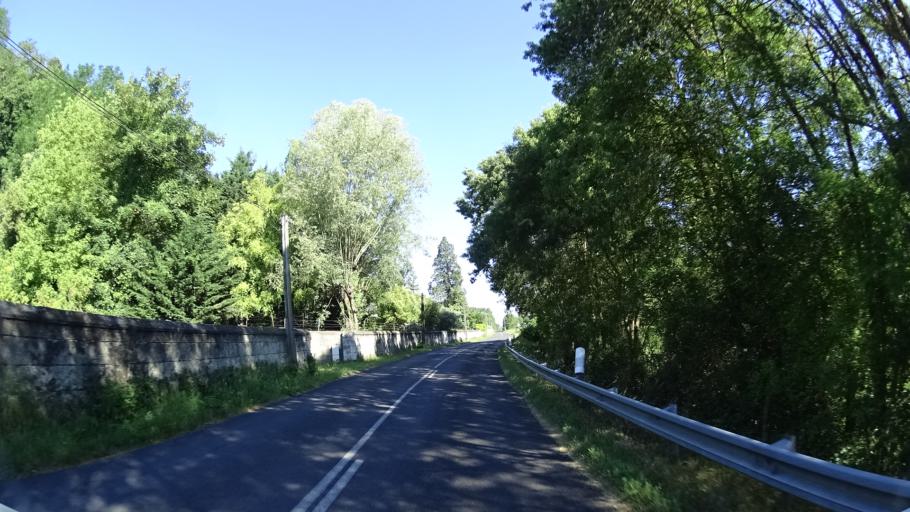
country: FR
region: Pays de la Loire
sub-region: Departement de Maine-et-Loire
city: Saint-Martin-de-la-Place
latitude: 47.2911
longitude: -0.1353
